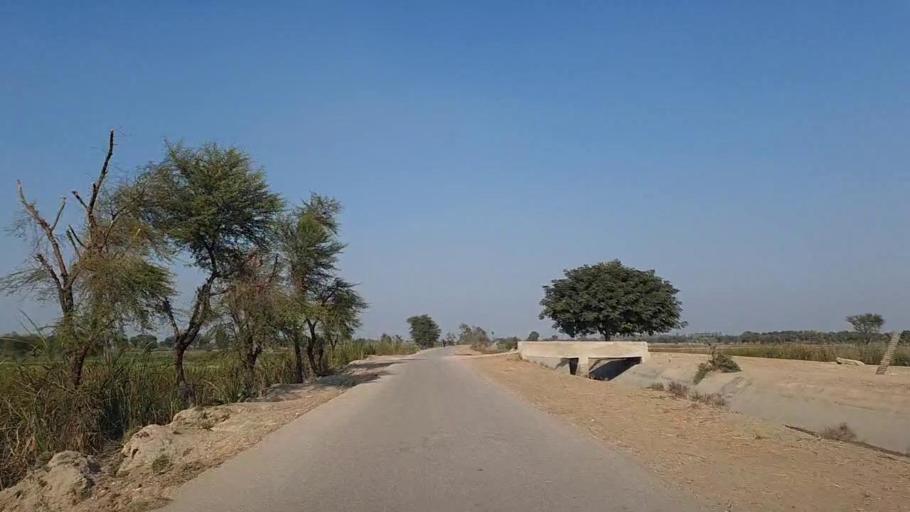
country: PK
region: Sindh
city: Daur
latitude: 26.4257
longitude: 68.2627
